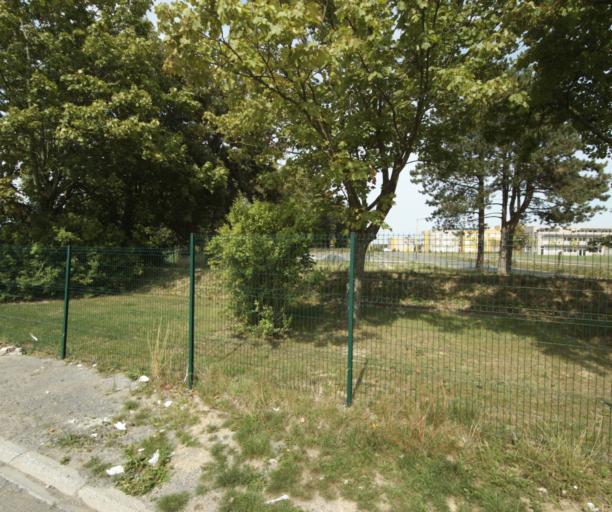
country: FR
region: Nord-Pas-de-Calais
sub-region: Departement du Nord
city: Wattignies
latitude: 50.5983
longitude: 3.0333
